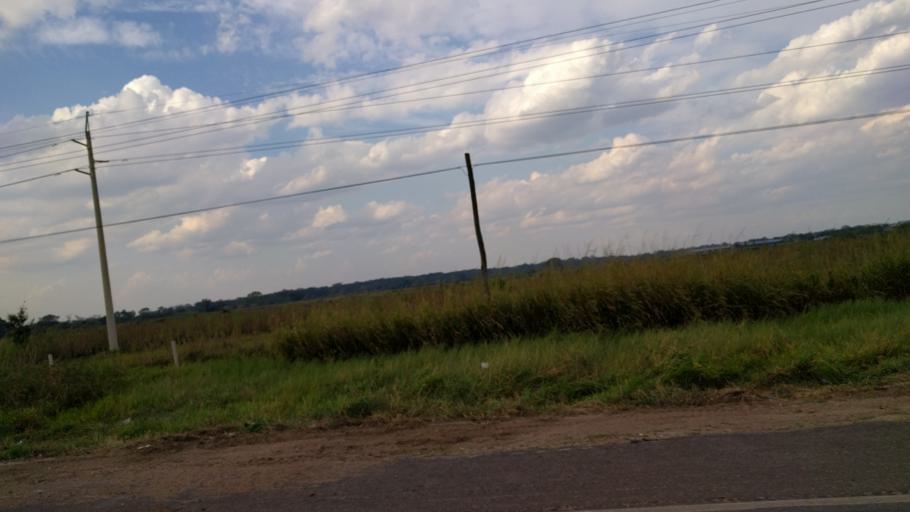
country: BO
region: Santa Cruz
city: Warnes
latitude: -17.4284
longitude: -63.1941
